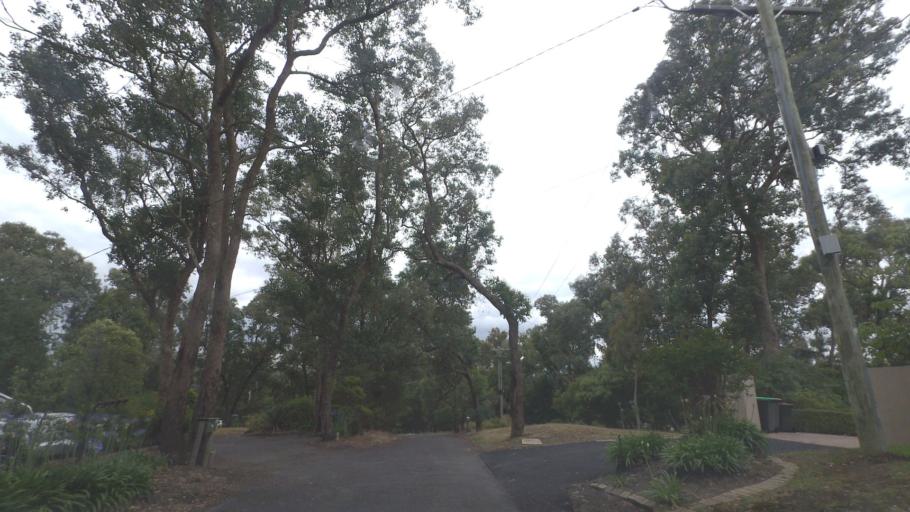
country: AU
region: Victoria
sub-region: Manningham
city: Warrandyte
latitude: -37.7556
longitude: 145.2158
